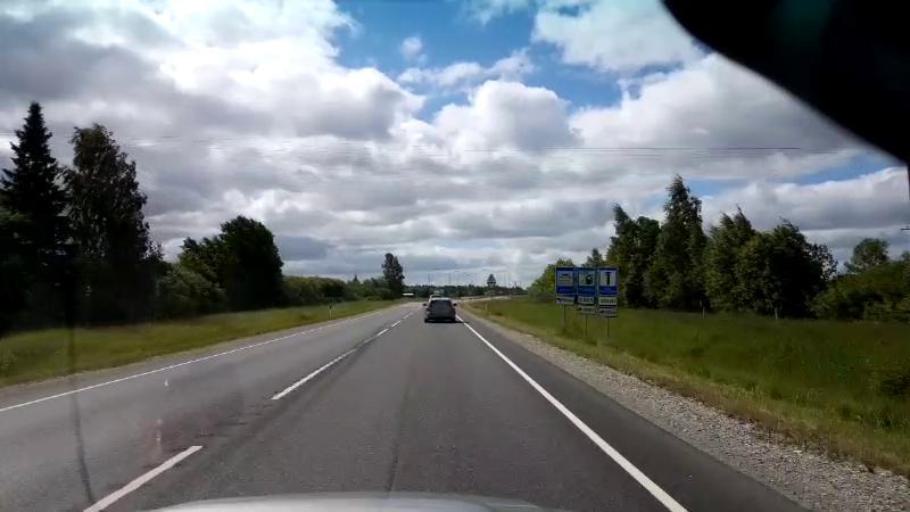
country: EE
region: Paernumaa
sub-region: Sauga vald
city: Sauga
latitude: 58.4316
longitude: 24.5008
